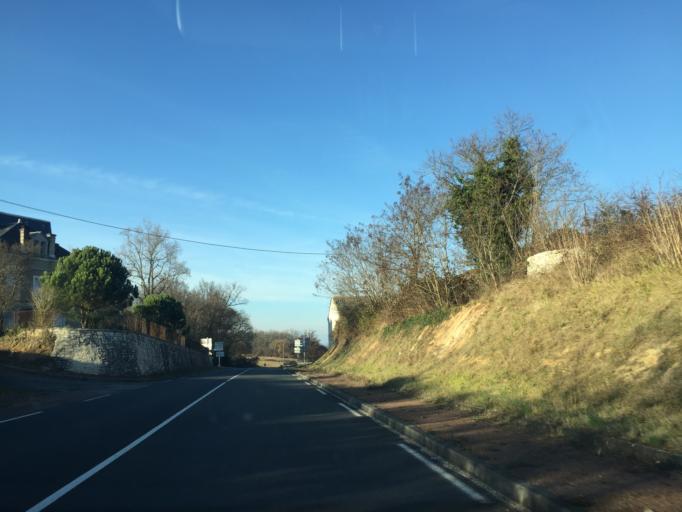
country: FR
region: Aquitaine
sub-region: Departement de la Dordogne
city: Riberac
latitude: 45.1987
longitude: 0.3679
